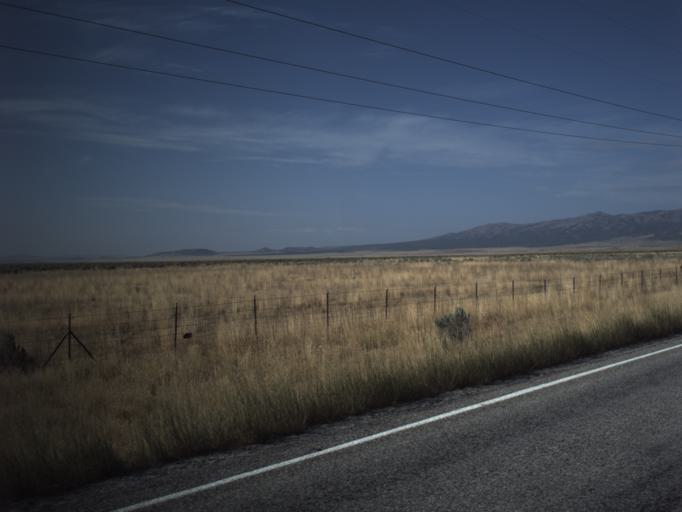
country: US
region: Idaho
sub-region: Oneida County
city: Malad City
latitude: 41.9656
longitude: -113.0220
